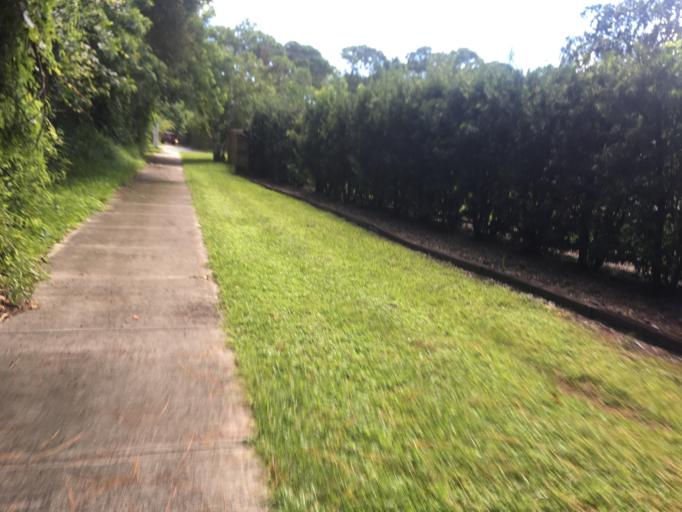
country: US
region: Florida
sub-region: Martin County
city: Palm City
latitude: 27.1756
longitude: -80.2701
